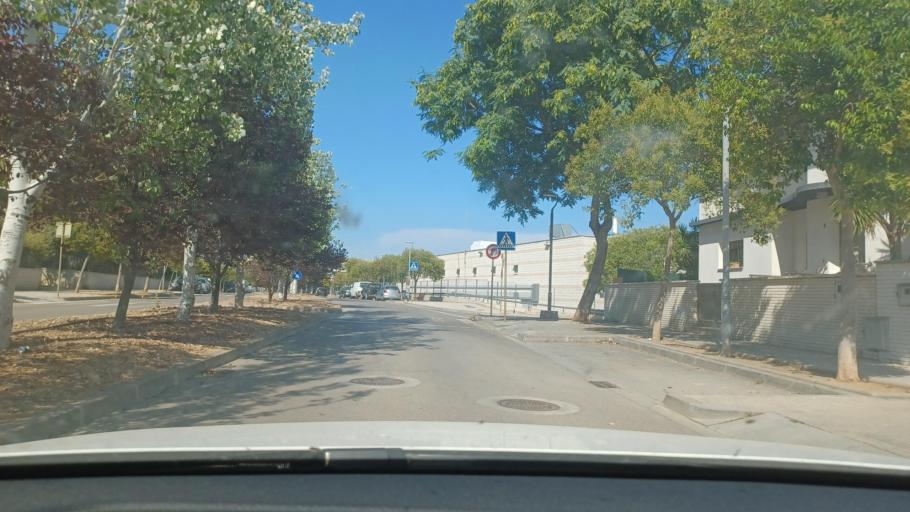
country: ES
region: Catalonia
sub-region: Provincia de Tarragona
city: Sant Carles de la Rapita
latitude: 40.6091
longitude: 0.5825
